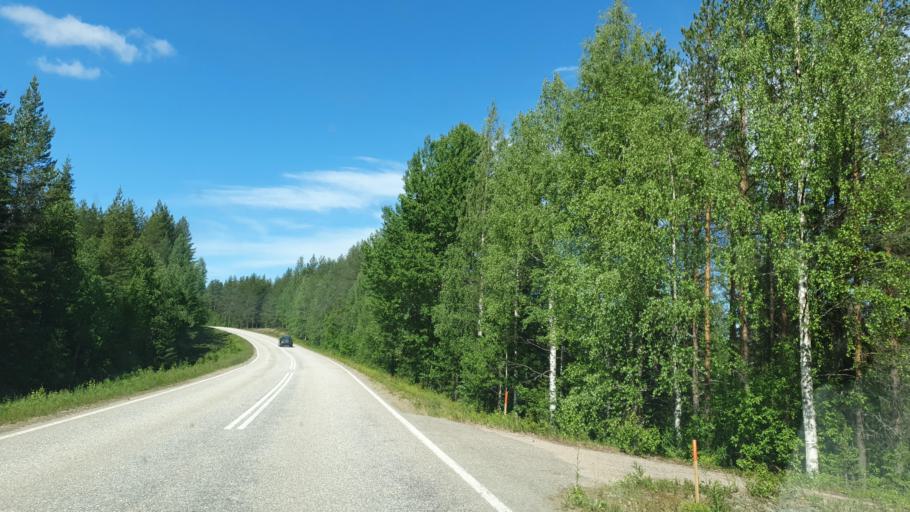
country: FI
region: Kainuu
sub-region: Kehys-Kainuu
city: Hyrynsalmi
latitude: 64.6065
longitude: 28.7059
